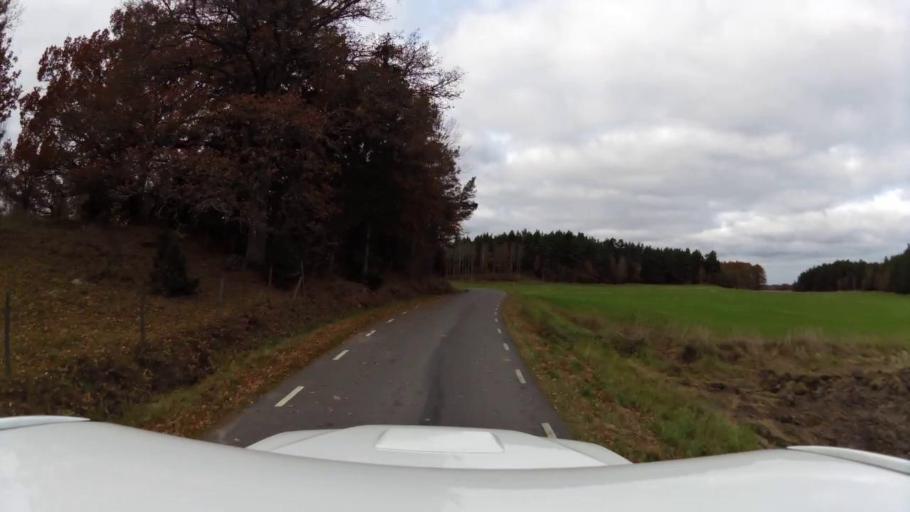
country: SE
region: OEstergoetland
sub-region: Linkopings Kommun
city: Linghem
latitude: 58.3915
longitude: 15.8069
